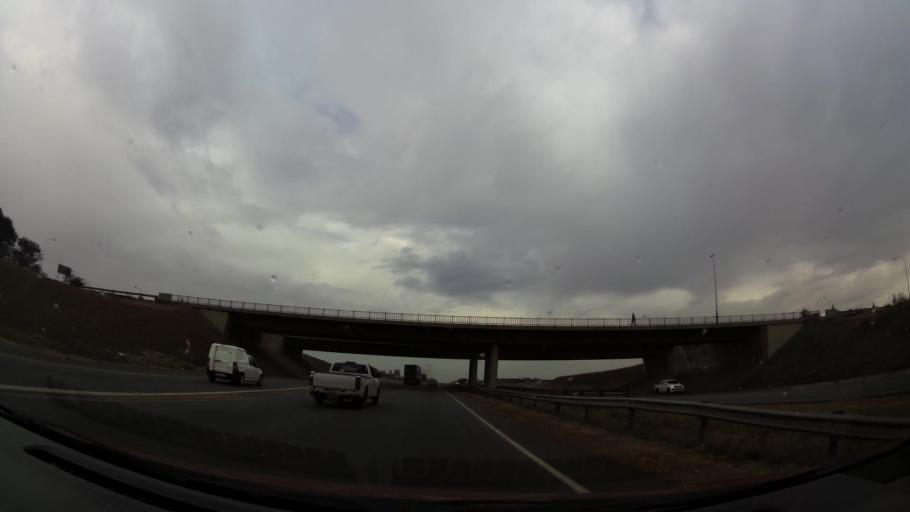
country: ZA
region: Gauteng
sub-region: City of Johannesburg Metropolitan Municipality
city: Soweto
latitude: -26.3023
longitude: 27.9225
